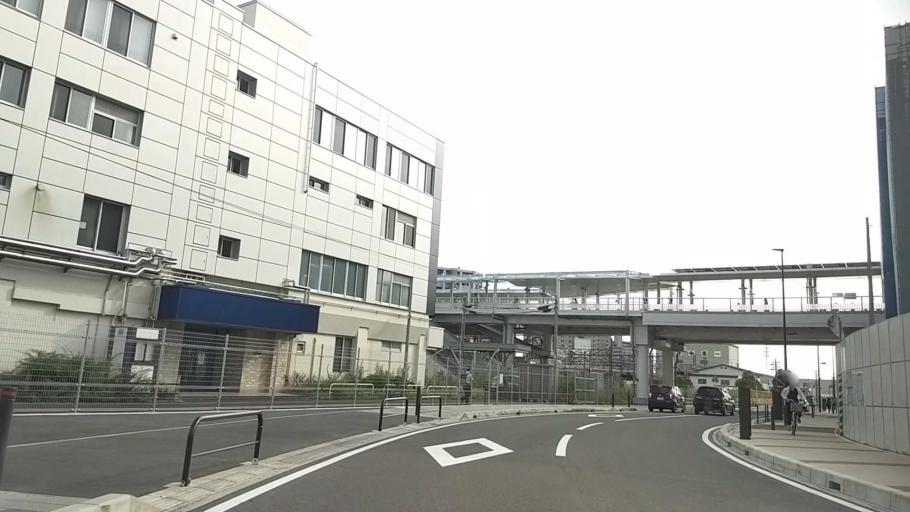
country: JP
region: Kanagawa
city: Atsugi
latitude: 35.4538
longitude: 139.3909
